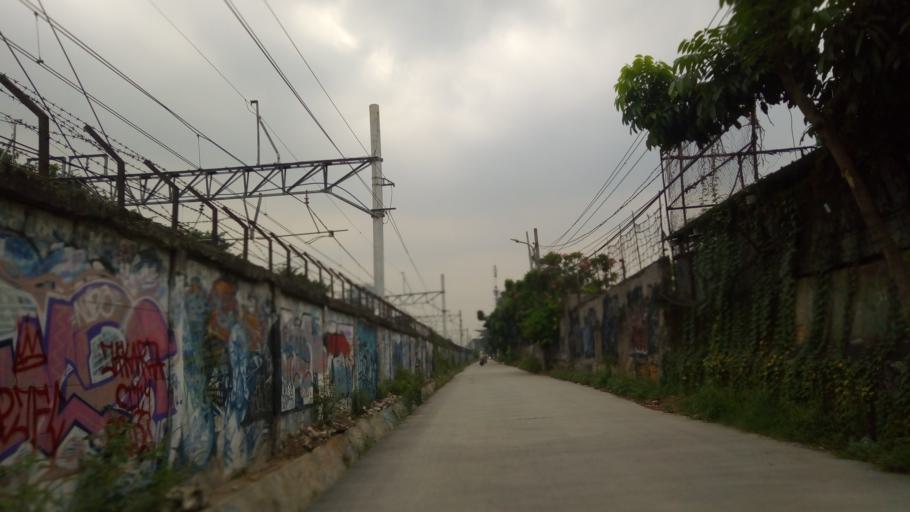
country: ID
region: Jakarta Raya
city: Jakarta
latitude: -6.1575
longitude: 106.8405
